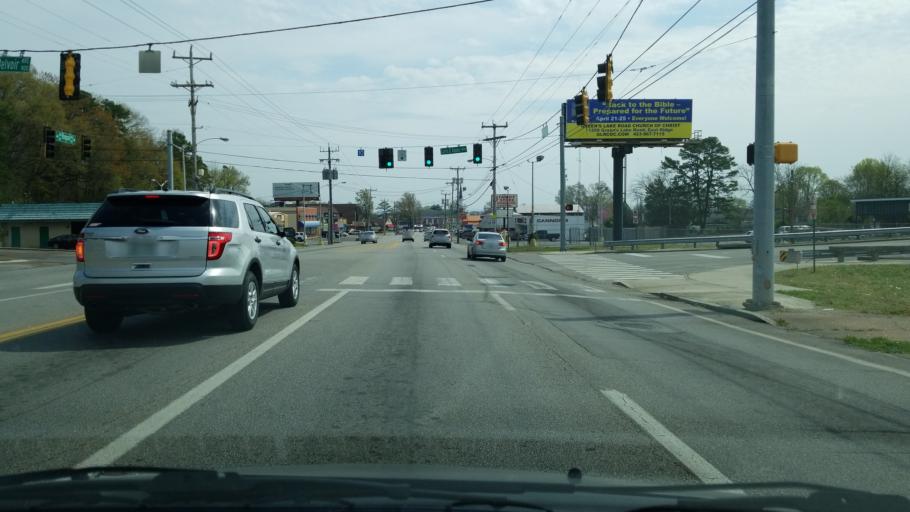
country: US
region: Tennessee
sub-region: Hamilton County
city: East Ridge
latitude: 34.9975
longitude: -85.2491
